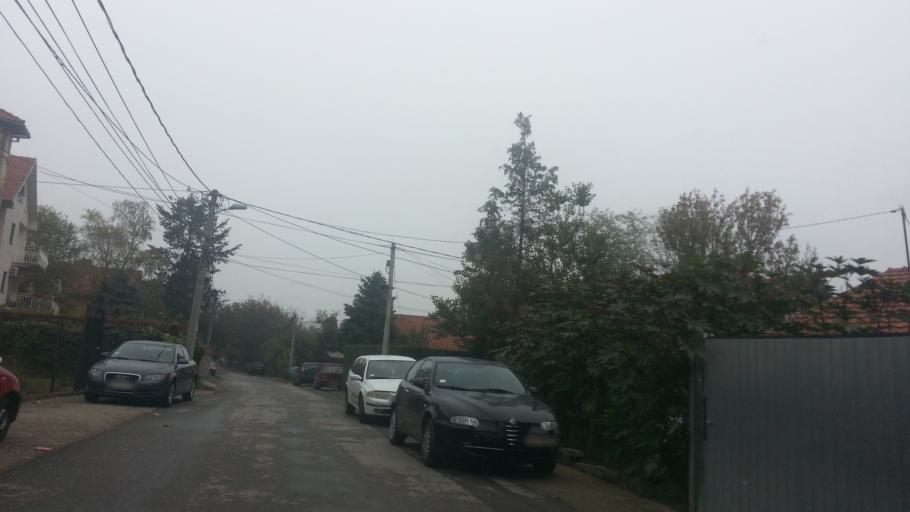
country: RS
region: Central Serbia
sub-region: Belgrade
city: Zemun
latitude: 44.8351
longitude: 20.3853
